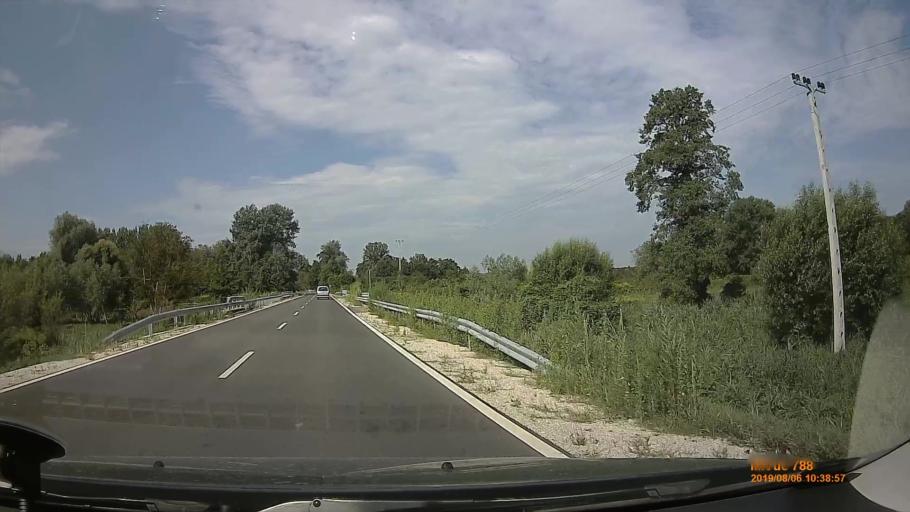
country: HU
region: Zala
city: Zalakomar
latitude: 46.5356
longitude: 17.1731
